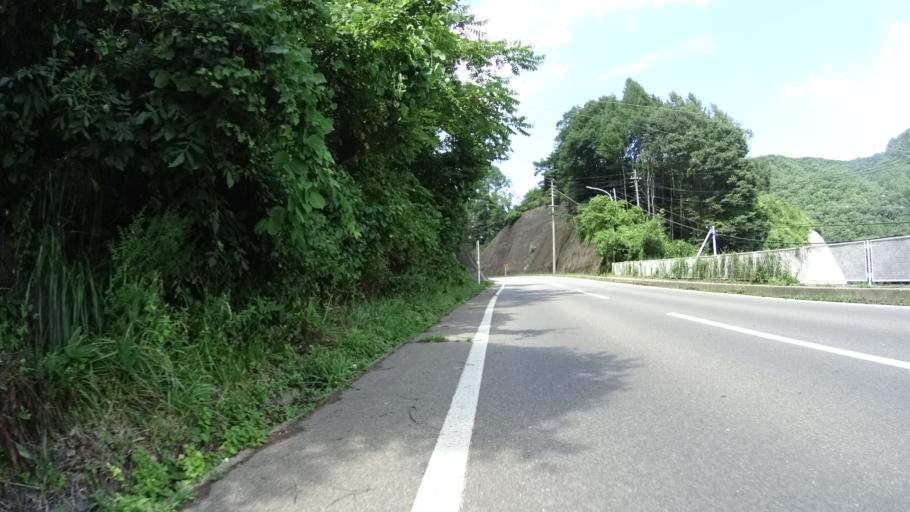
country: JP
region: Nagano
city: Saku
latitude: 36.0808
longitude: 138.4880
